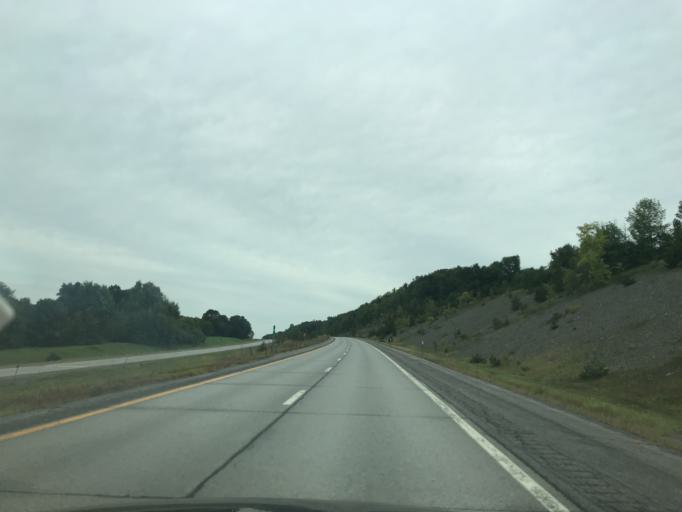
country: US
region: New York
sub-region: Schoharie County
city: Schoharie
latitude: 42.6827
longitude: -74.3680
